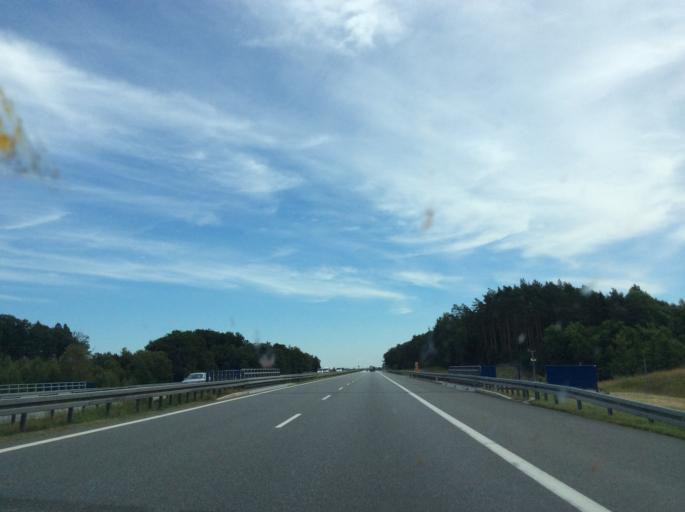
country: PL
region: Greater Poland Voivodeship
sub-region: Powiat nowotomyski
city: Kuslin
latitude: 52.3774
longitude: 16.2722
